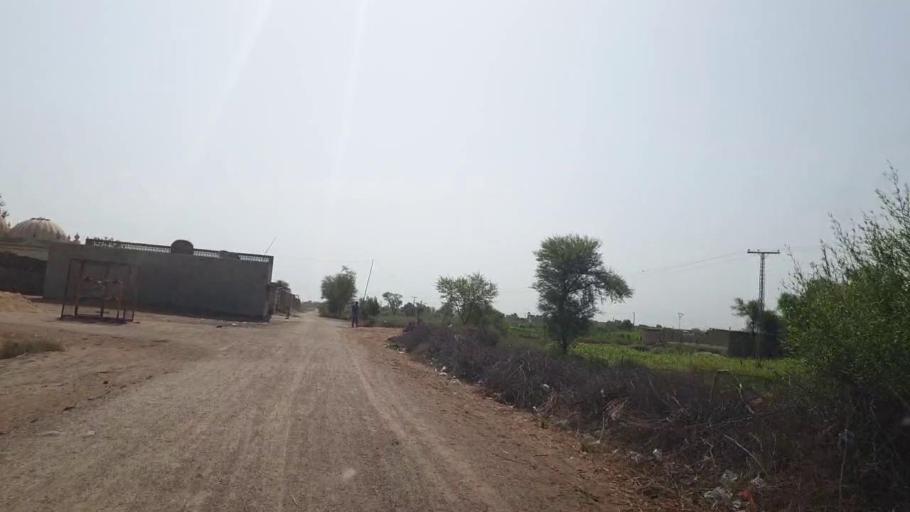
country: PK
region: Sindh
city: Daur
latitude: 26.3194
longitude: 68.2177
